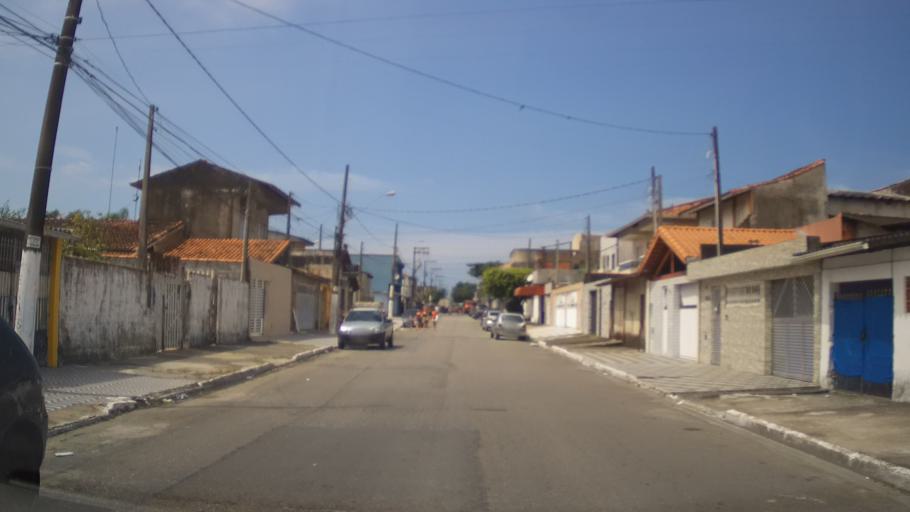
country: BR
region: Sao Paulo
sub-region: Praia Grande
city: Praia Grande
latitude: -24.0194
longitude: -46.4882
